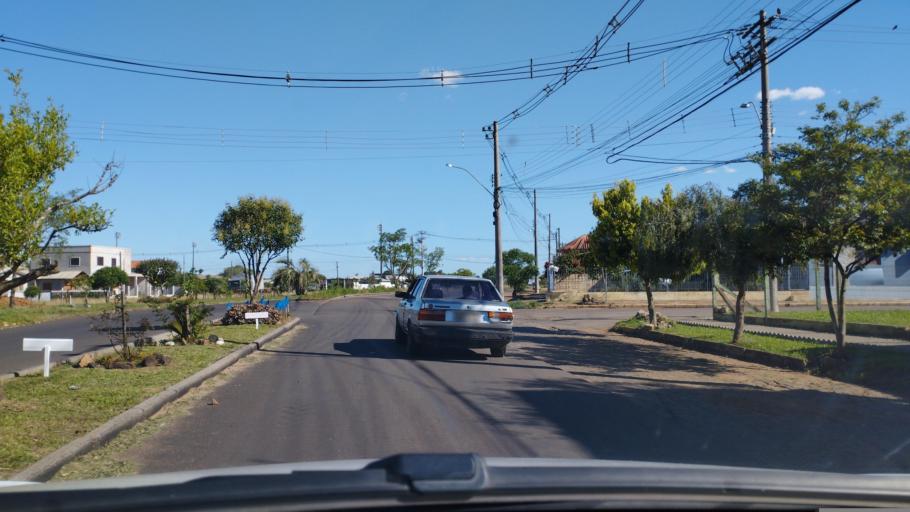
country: BR
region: Rio Grande do Sul
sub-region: Tupancireta
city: Tupancireta
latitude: -29.0753
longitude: -53.8370
